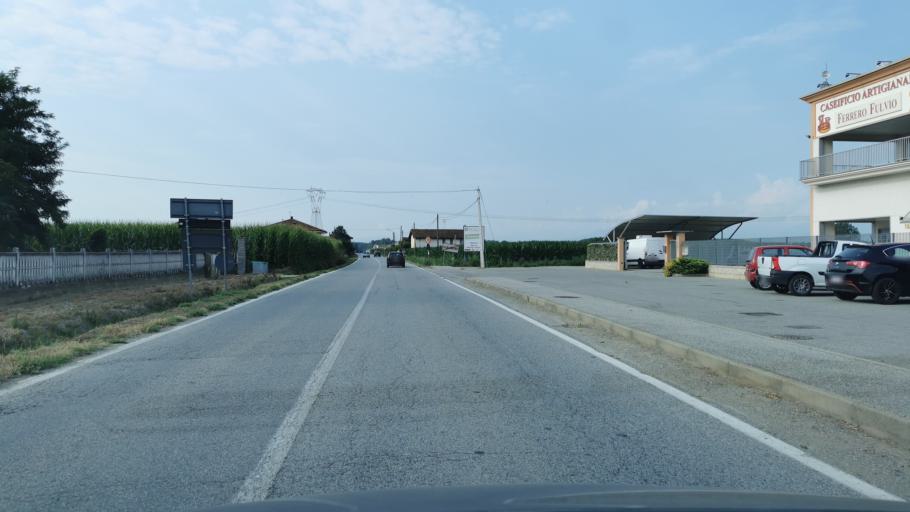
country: IT
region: Piedmont
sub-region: Provincia di Torino
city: Scalenghe
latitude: 44.8848
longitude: 7.4955
